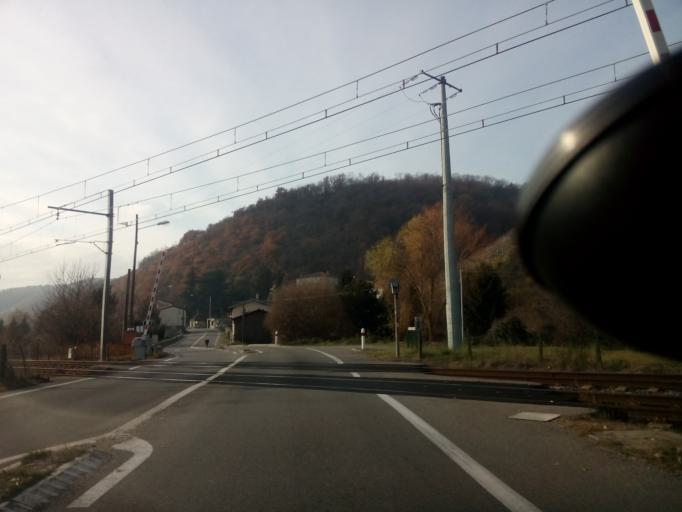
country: FR
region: Rhone-Alpes
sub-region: Departement de l'Isere
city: Les Roches-de-Condrieu
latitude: 45.4399
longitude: 4.7492
